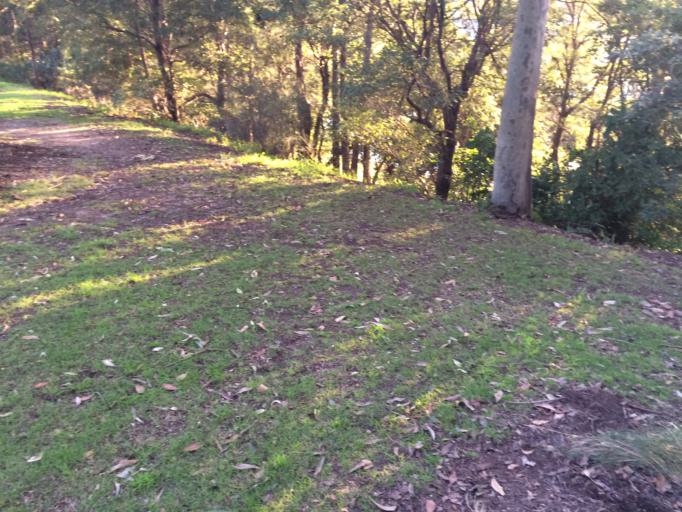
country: AU
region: New South Wales
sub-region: Lane Cove
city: Greenwich
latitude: -33.8372
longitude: 151.1843
